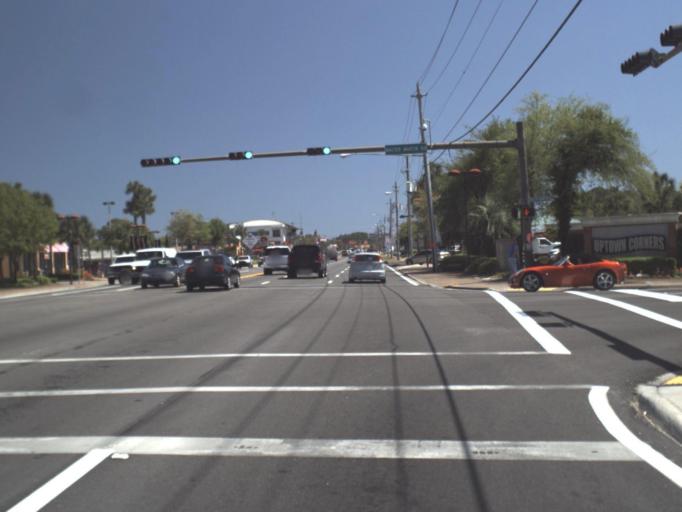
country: US
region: Florida
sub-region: Okaloosa County
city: Fort Walton Beach
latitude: 30.4178
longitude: -86.6084
